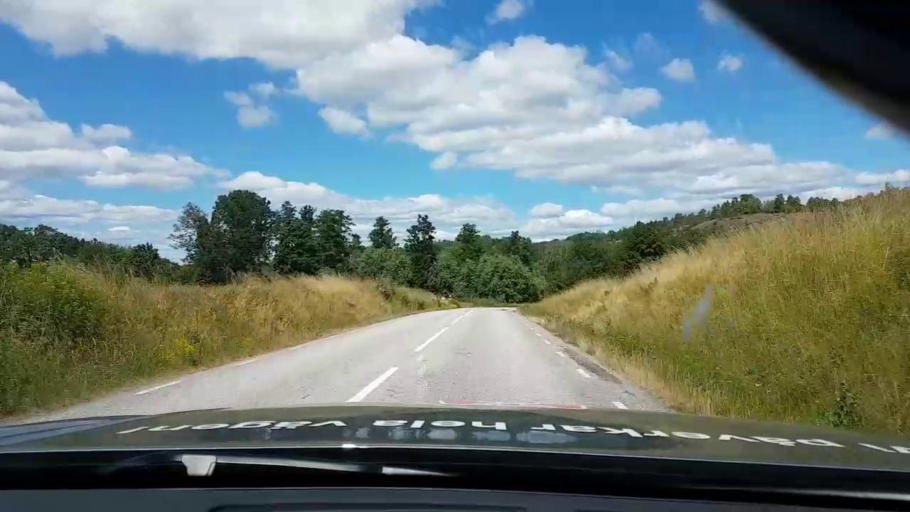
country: SE
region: Kalmar
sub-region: Vasterviks Kommun
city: Overum
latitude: 58.0531
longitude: 16.4057
